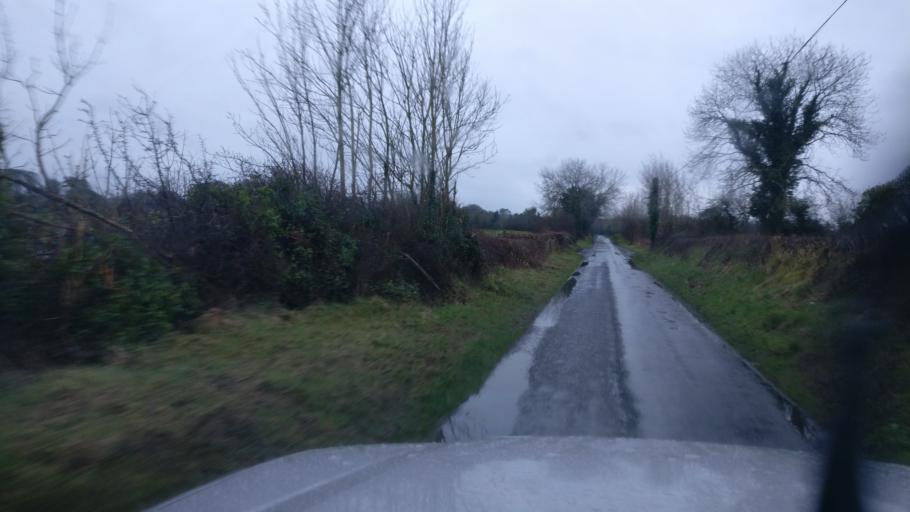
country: IE
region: Connaught
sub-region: County Galway
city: Ballinasloe
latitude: 53.2848
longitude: -8.2987
